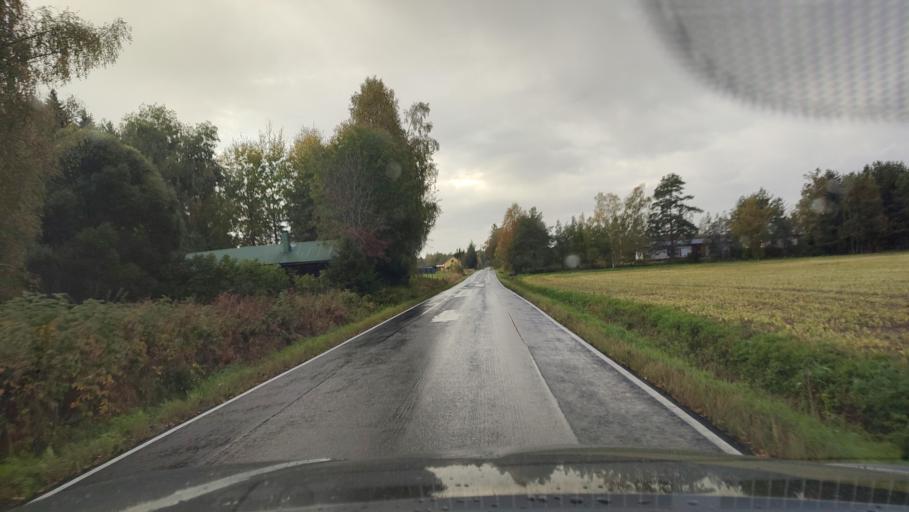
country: FI
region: Southern Ostrobothnia
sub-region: Suupohja
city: Karijoki
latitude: 62.3140
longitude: 21.6984
